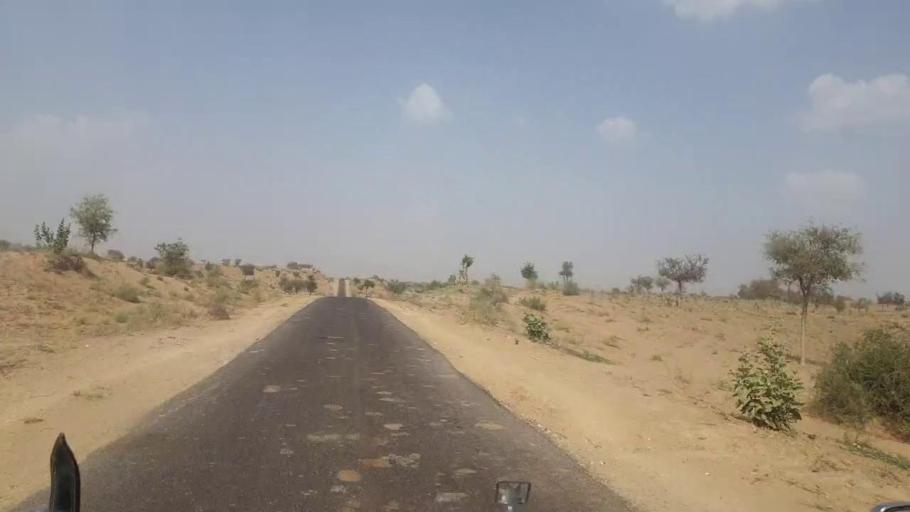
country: PK
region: Sindh
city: Islamkot
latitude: 25.1631
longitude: 70.2863
